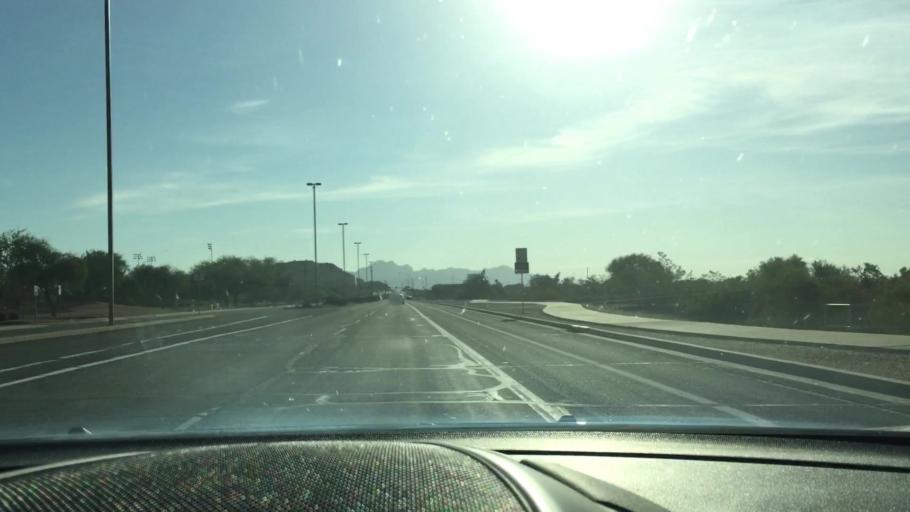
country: US
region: Arizona
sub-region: Pinal County
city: Apache Junction
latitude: 33.4367
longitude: -111.6635
